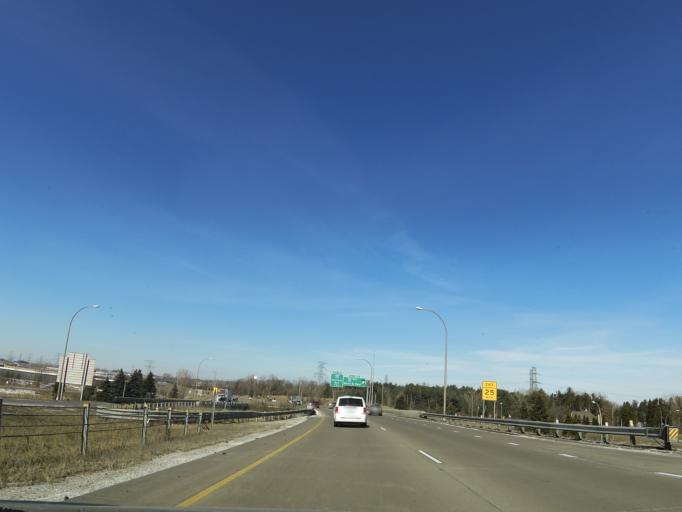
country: US
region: Minnesota
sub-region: Ramsey County
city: North Saint Paul
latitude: 45.0291
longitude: -92.9611
